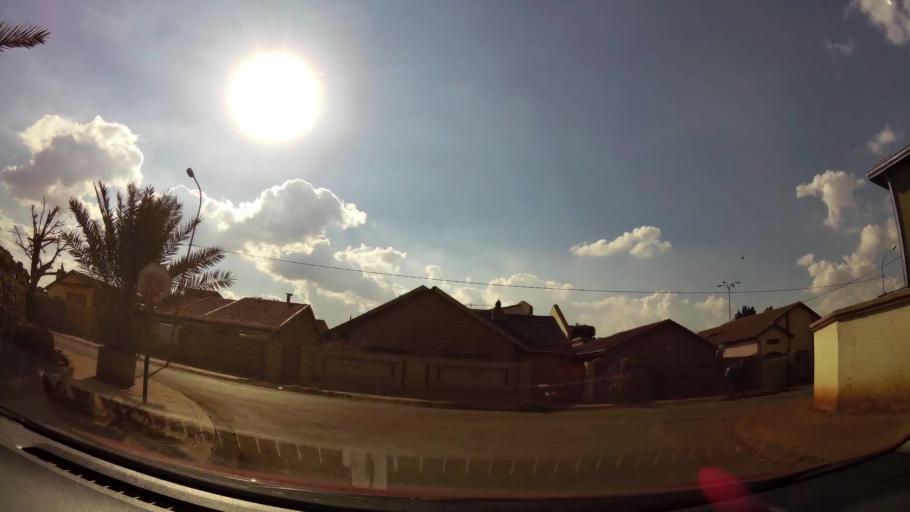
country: ZA
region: Gauteng
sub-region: City of Johannesburg Metropolitan Municipality
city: Soweto
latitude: -26.2224
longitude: 27.8622
